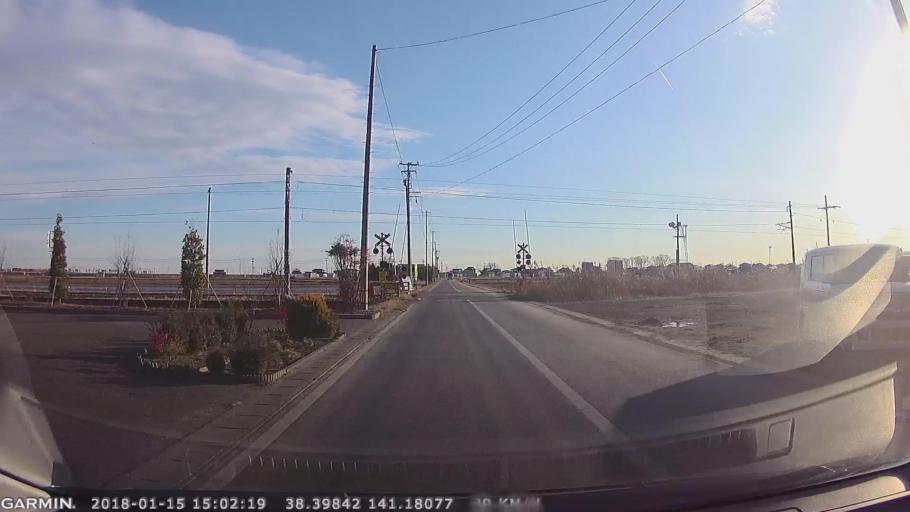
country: JP
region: Miyagi
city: Yamoto
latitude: 38.3984
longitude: 141.1807
